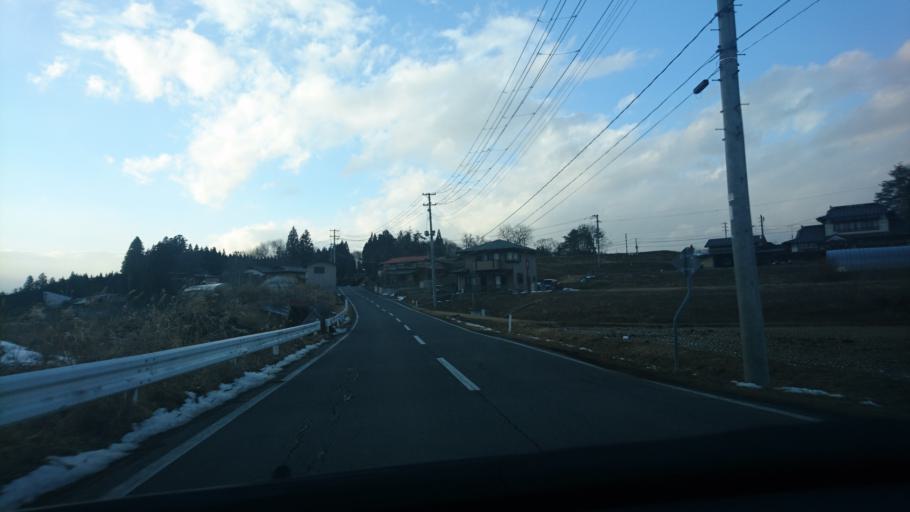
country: JP
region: Iwate
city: Ichinoseki
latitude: 39.0088
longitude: 141.3293
